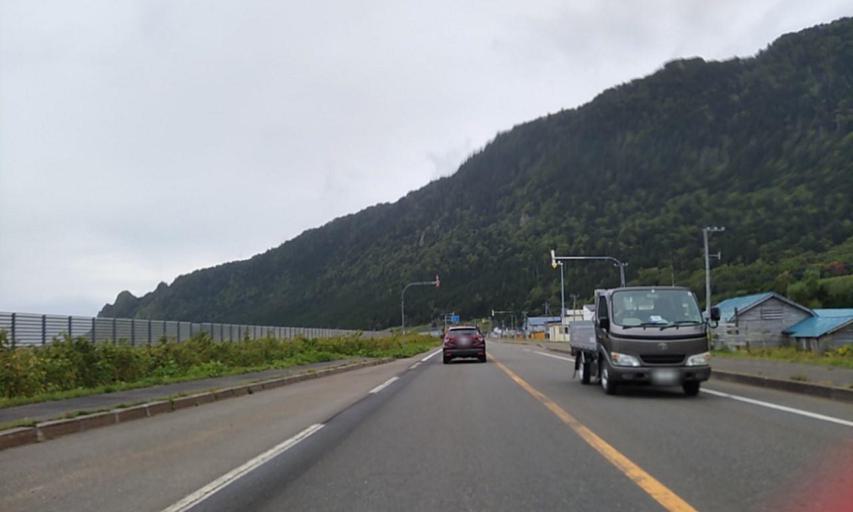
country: JP
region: Hokkaido
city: Nayoro
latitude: 45.0626
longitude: 142.4792
